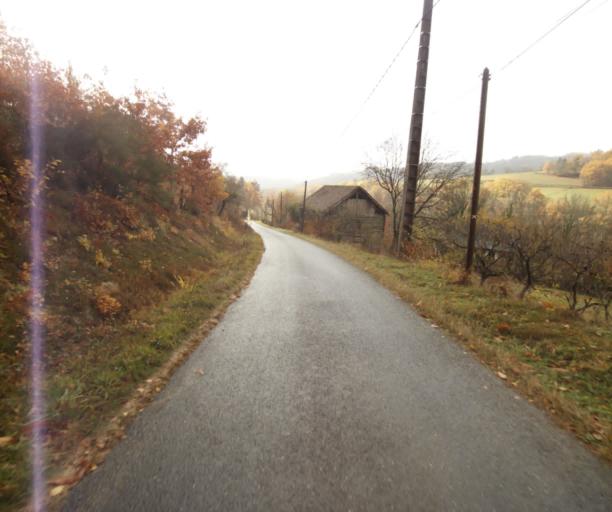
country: FR
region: Limousin
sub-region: Departement de la Correze
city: Cornil
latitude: 45.2100
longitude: 1.6588
